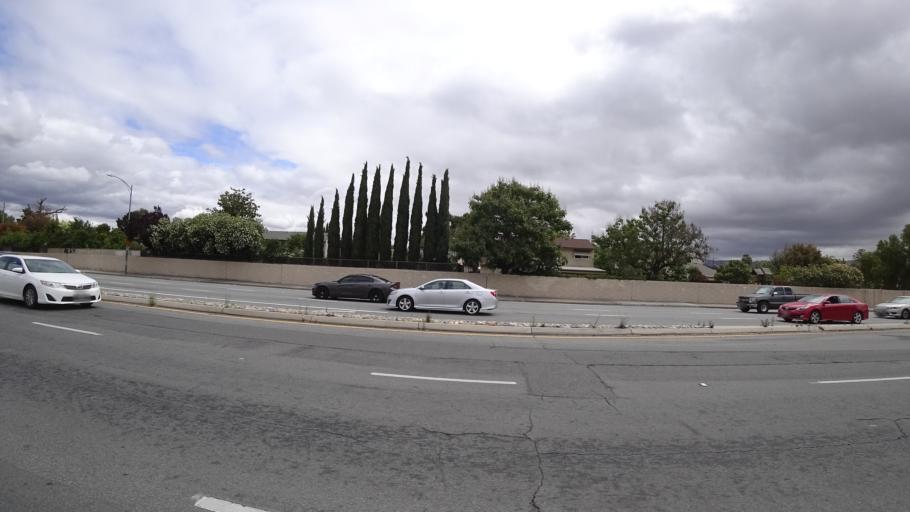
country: US
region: California
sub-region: Santa Clara County
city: Seven Trees
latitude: 37.2972
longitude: -121.8372
